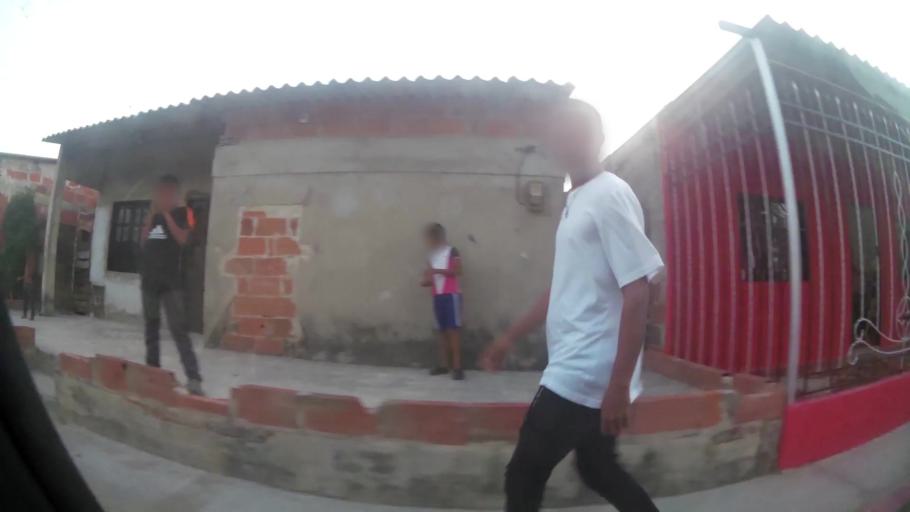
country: CO
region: Atlantico
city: Barranquilla
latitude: 10.9520
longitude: -74.8304
